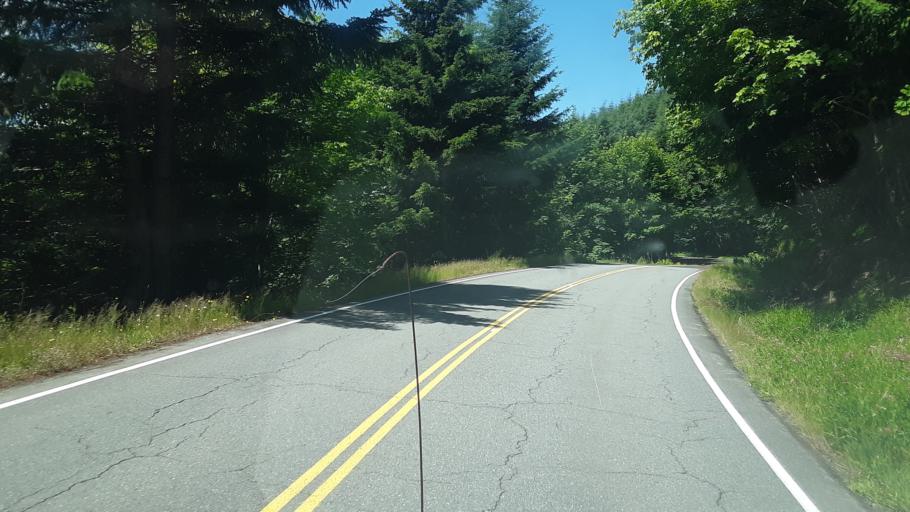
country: US
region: Washington
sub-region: Clark County
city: Yacolt
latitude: 46.0627
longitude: -122.1131
